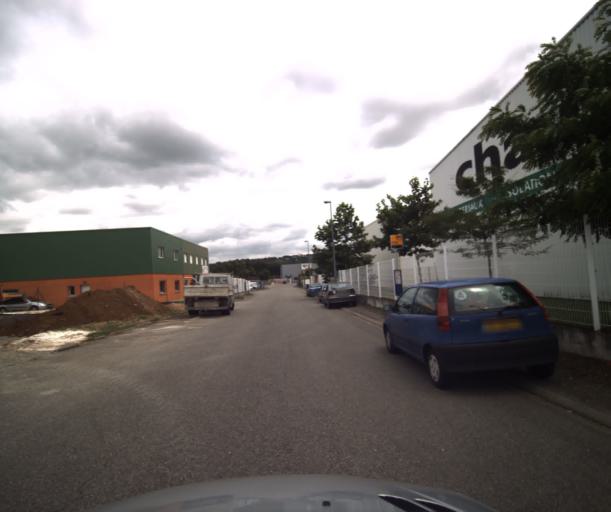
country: FR
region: Midi-Pyrenees
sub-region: Departement de la Haute-Garonne
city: Lacroix-Falgarde
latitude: 43.4907
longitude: 1.3950
